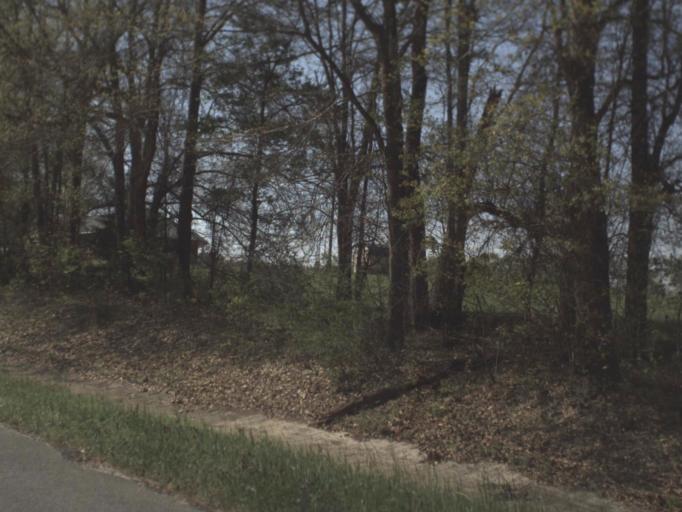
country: US
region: Florida
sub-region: Washington County
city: Chipley
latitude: 30.8491
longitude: -85.5008
